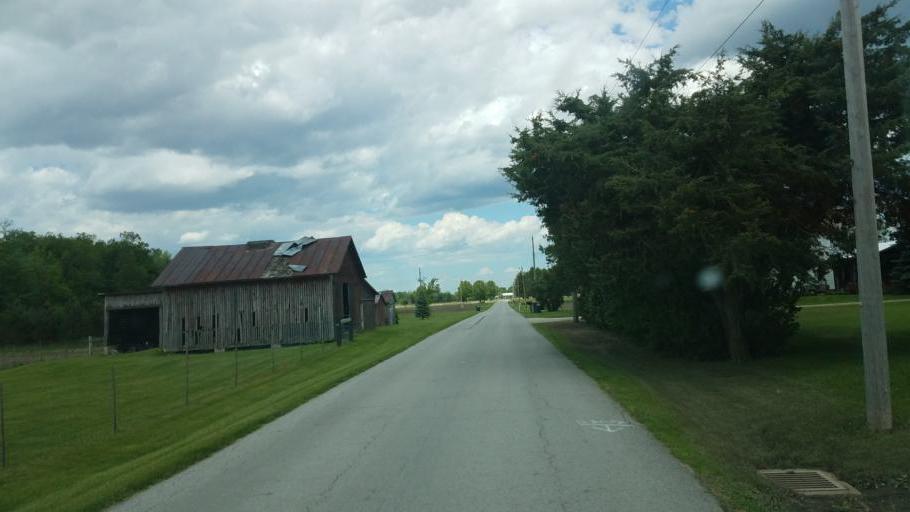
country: US
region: Ohio
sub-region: Huron County
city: Monroeville
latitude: 41.2666
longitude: -82.6782
